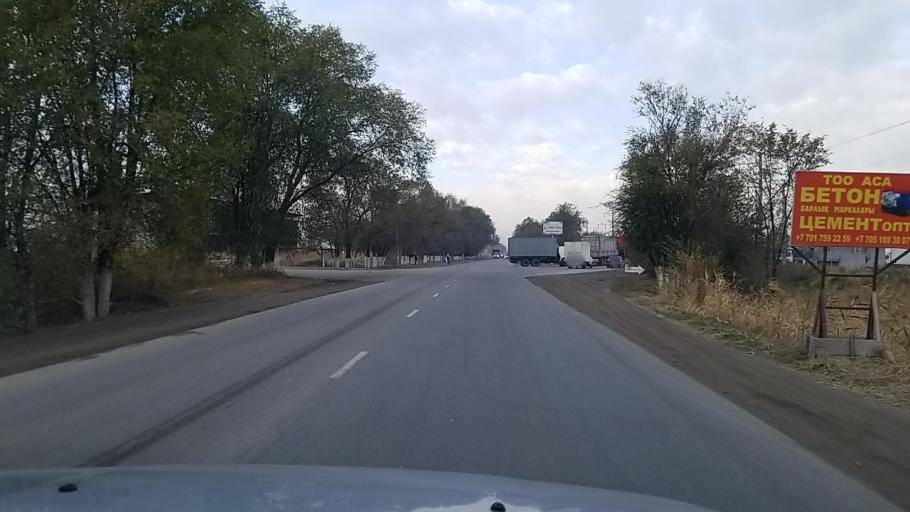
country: KZ
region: Almaty Oblysy
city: Burunday
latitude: 43.3562
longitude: 76.7945
